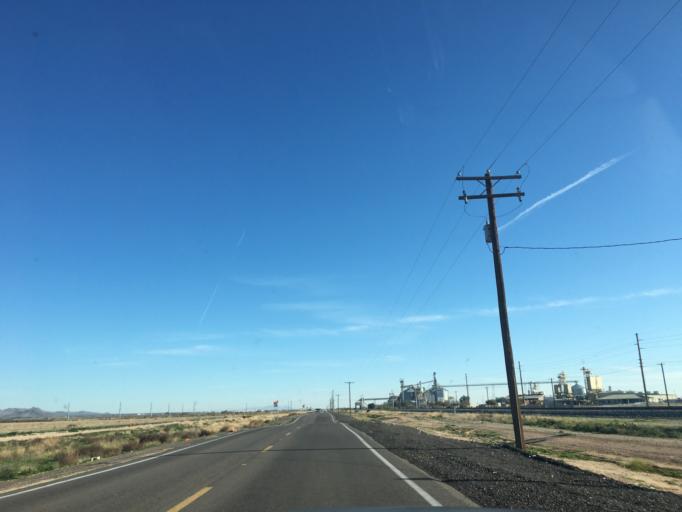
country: US
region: Arizona
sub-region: Pinal County
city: Maricopa
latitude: 33.0191
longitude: -111.9870
